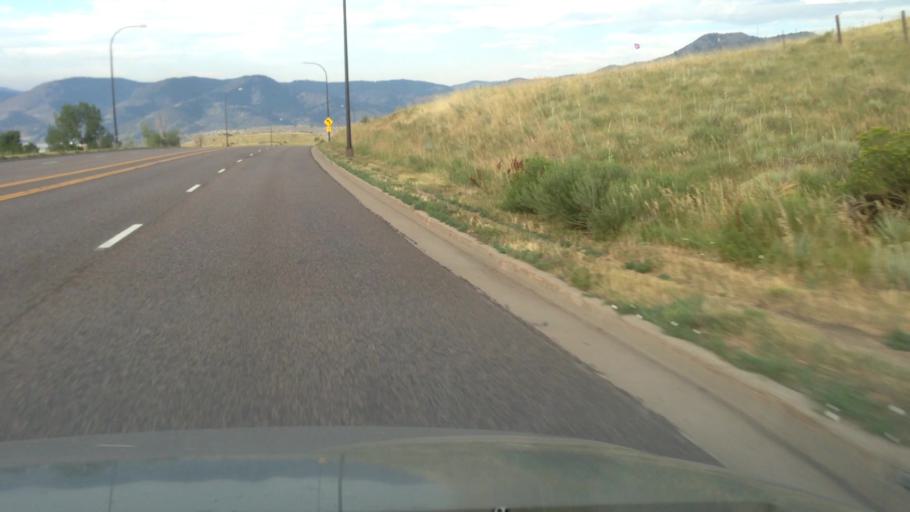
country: US
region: Colorado
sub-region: Jefferson County
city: West Pleasant View
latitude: 39.6844
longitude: -105.1573
